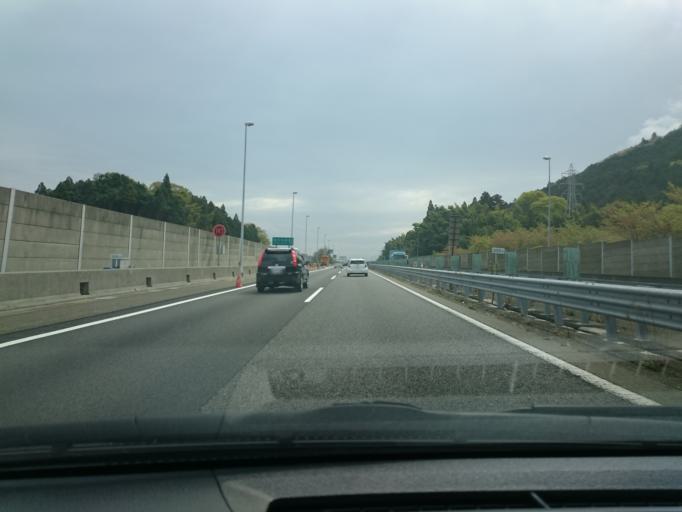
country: JP
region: Shiga Prefecture
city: Nagahama
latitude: 35.3327
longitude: 136.3794
